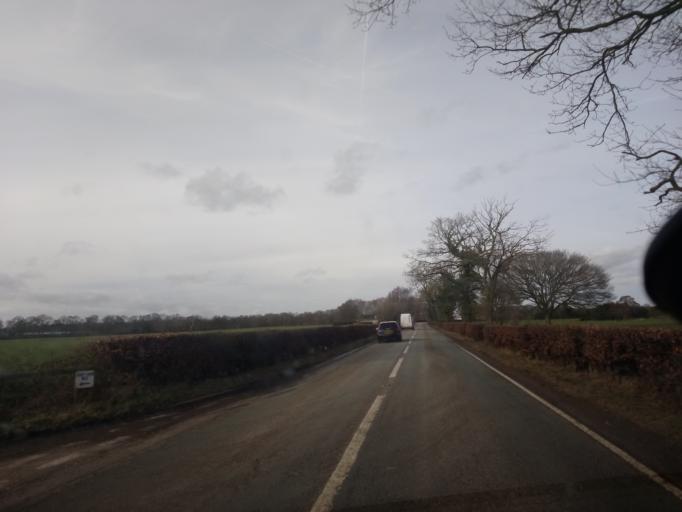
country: GB
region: England
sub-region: Shropshire
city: Prees
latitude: 52.8827
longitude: -2.6287
